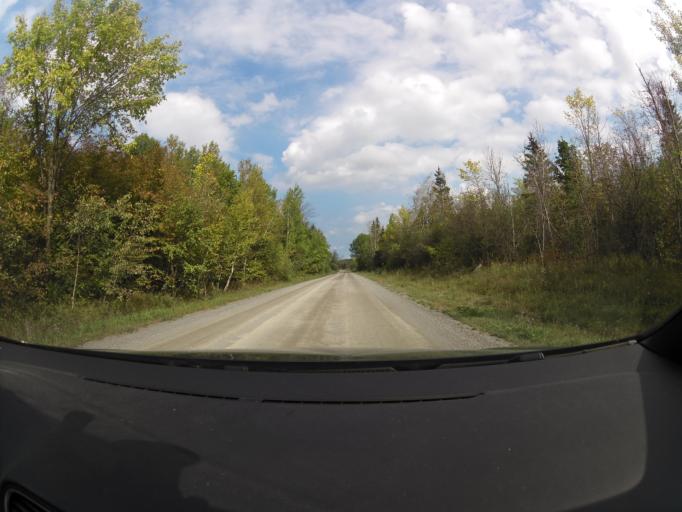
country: CA
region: Ontario
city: Arnprior
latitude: 45.3621
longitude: -76.1771
